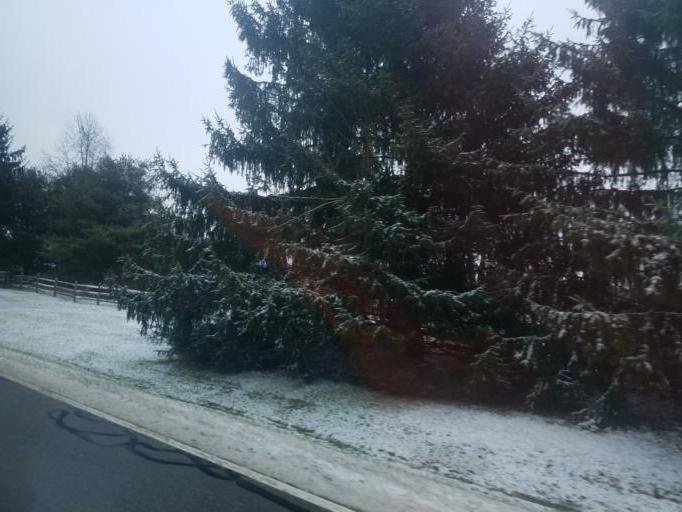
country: US
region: Ohio
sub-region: Franklin County
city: New Albany
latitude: 40.0688
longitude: -82.7939
